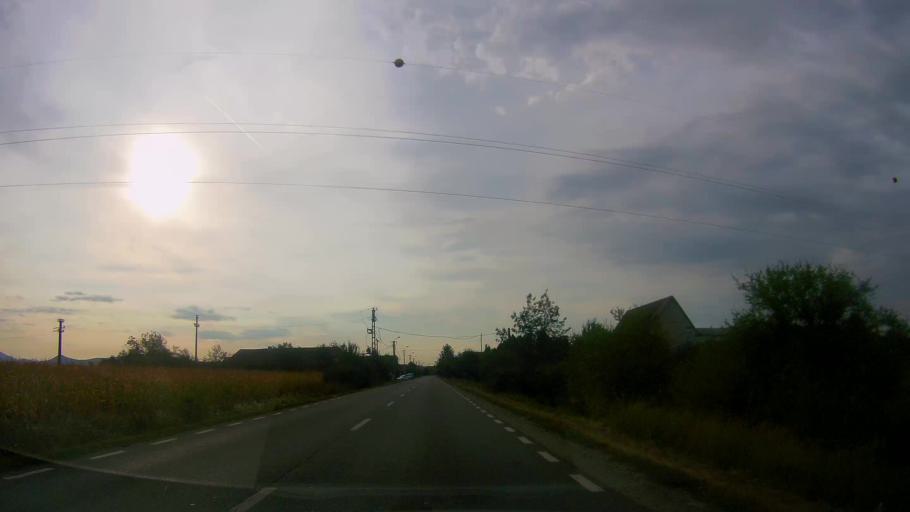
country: RO
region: Satu Mare
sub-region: Comuna Turulung
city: Turulung
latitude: 47.9478
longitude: 23.0707
